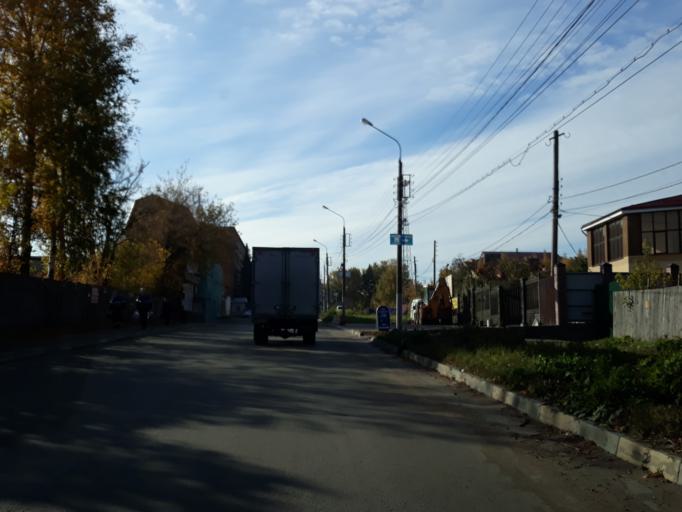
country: RU
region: Nizjnij Novgorod
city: Nizhniy Novgorod
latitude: 56.2433
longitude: 43.9846
